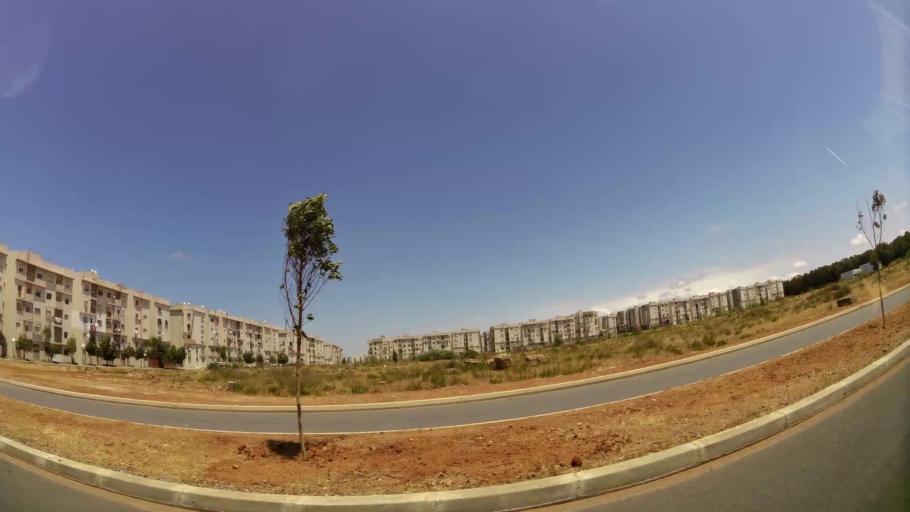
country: MA
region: Gharb-Chrarda-Beni Hssen
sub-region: Kenitra Province
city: Kenitra
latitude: 34.2484
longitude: -6.6412
